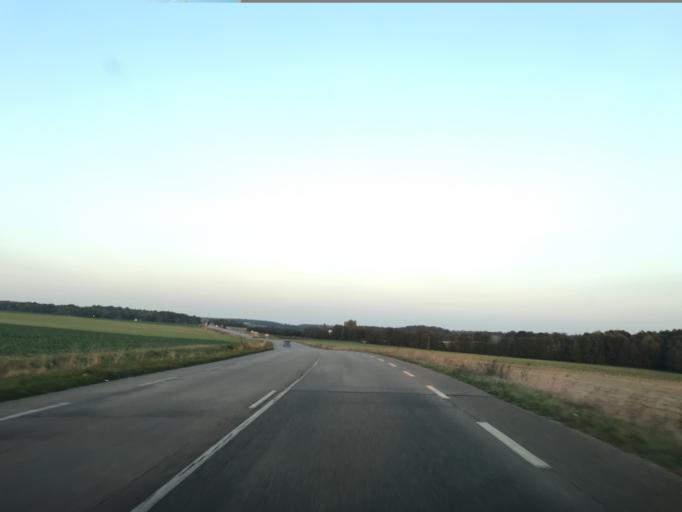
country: FR
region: Haute-Normandie
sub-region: Departement de l'Eure
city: Bourth
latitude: 48.7041
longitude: 0.8398
